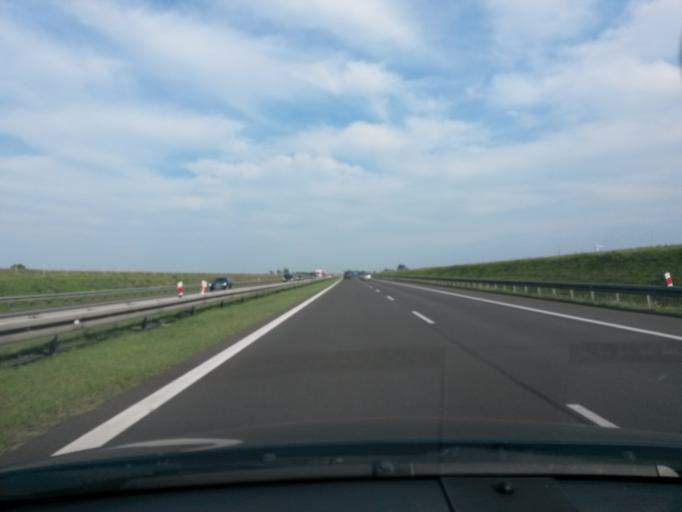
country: PL
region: Greater Poland Voivodeship
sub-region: Powiat slupecki
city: Ladek
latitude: 52.2171
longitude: 17.9679
